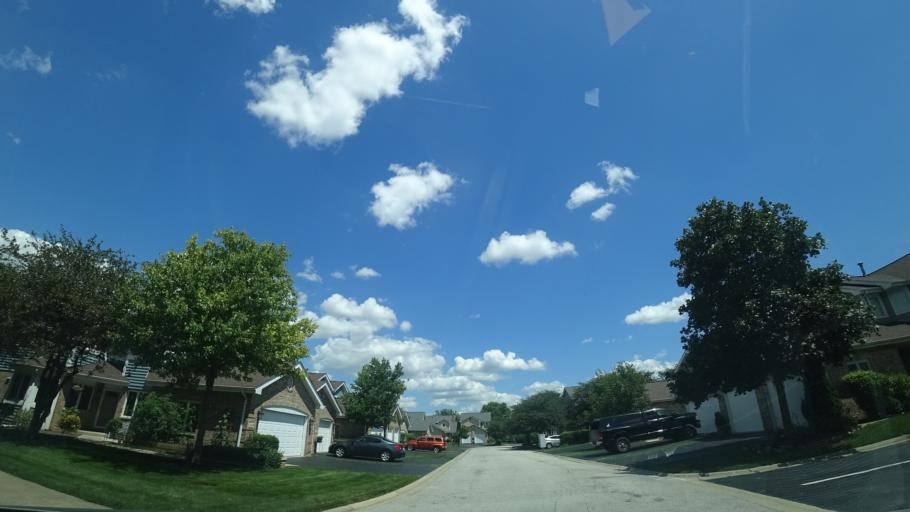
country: US
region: Illinois
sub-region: Will County
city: Mokena
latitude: 41.5748
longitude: -87.8938
